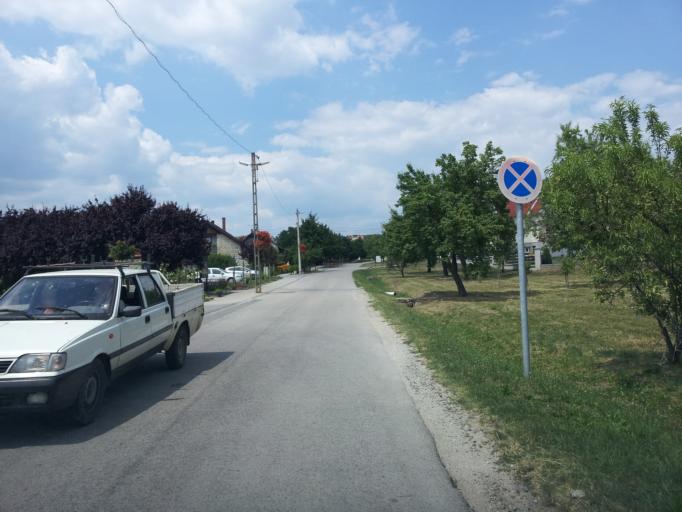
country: HU
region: Veszprem
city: Zanka
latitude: 46.8827
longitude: 17.7498
